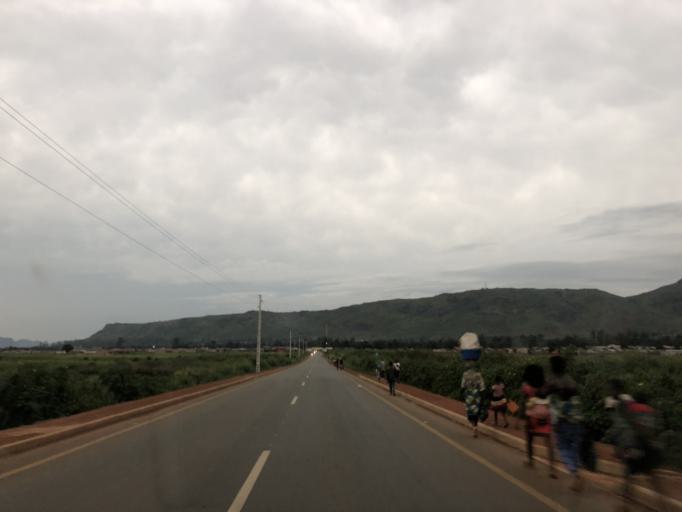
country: AO
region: Cuanza Sul
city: Uacu Cungo
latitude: -11.3405
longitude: 15.1035
